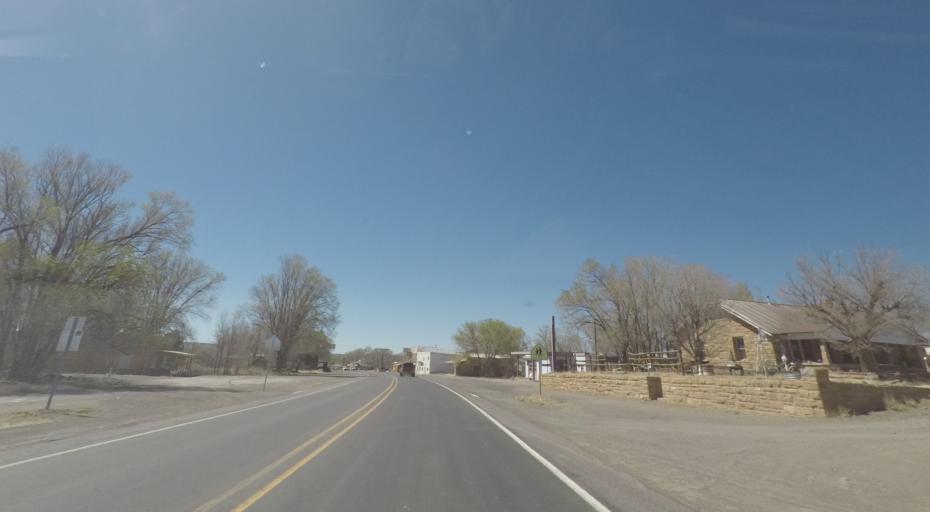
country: US
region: New Mexico
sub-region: Catron County
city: Reserve
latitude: 34.3423
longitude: -108.4938
